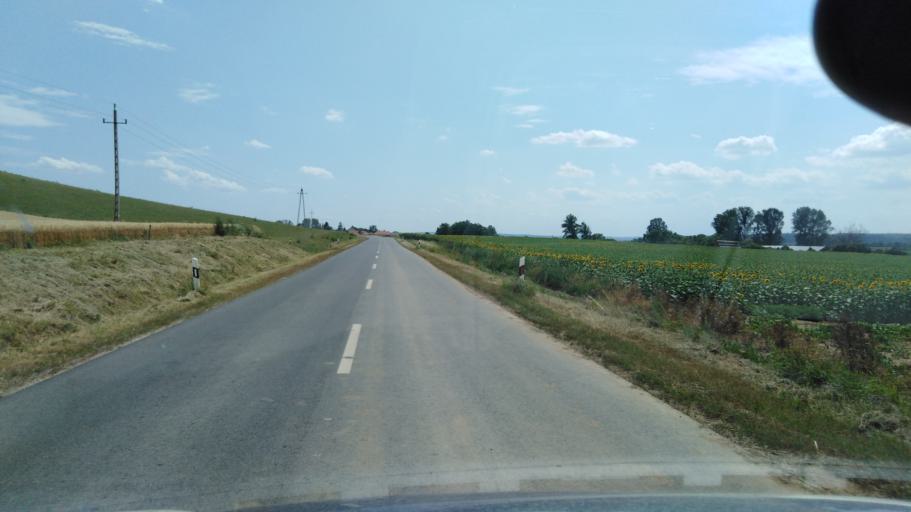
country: HU
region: Nograd
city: Szecseny
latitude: 48.1588
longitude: 19.5347
